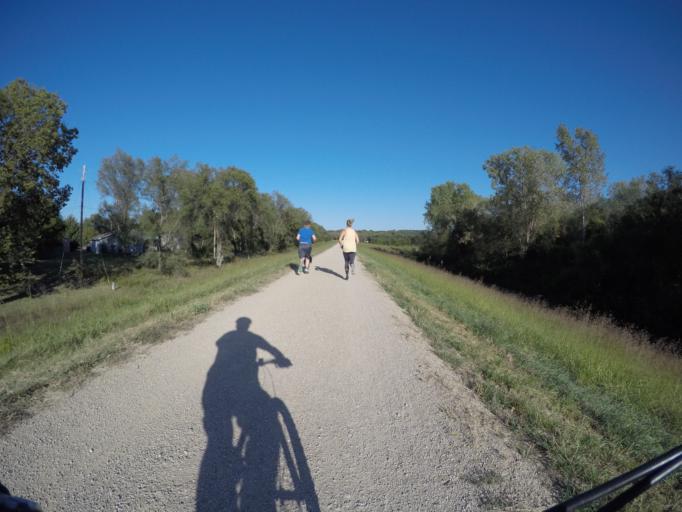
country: US
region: Kansas
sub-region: Riley County
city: Manhattan
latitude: 39.1709
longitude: -96.5700
